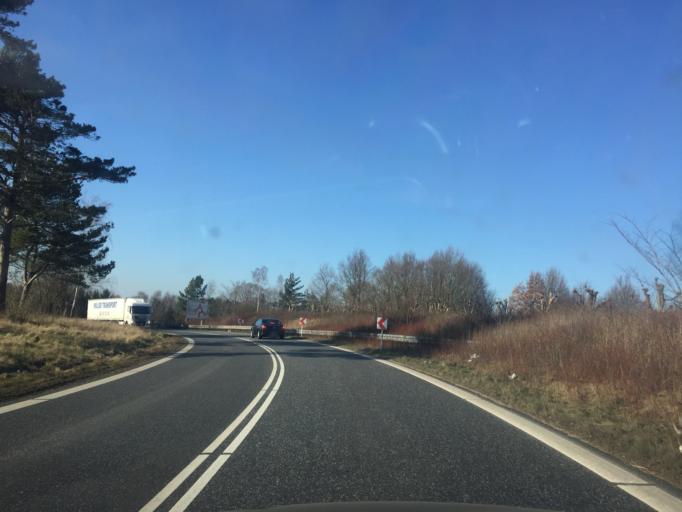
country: DK
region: Capital Region
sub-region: Horsholm Kommune
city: Horsholm
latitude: 55.8775
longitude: 12.4828
